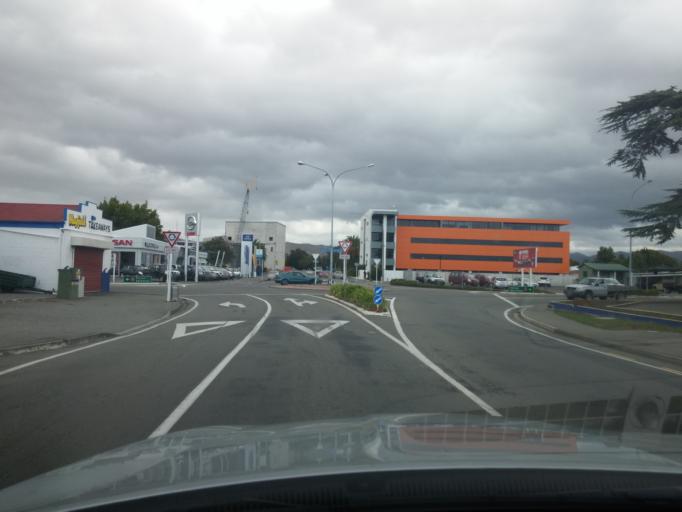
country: NZ
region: Marlborough
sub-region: Marlborough District
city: Blenheim
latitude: -41.5077
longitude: 173.9557
